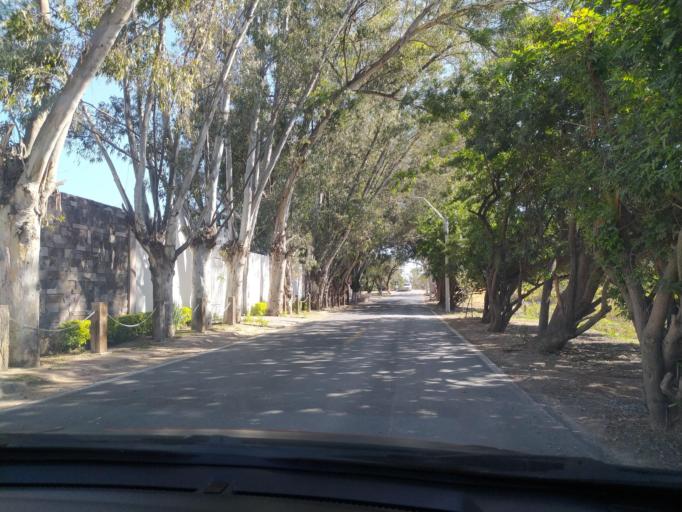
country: LA
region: Oudomxai
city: Muang La
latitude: 21.0461
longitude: 101.8355
